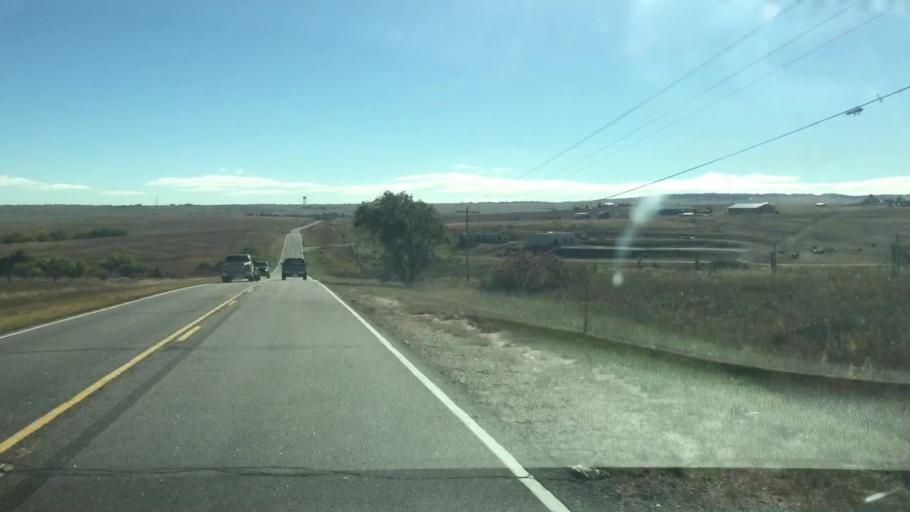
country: US
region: Colorado
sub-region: Elbert County
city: Kiowa
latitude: 39.3521
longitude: -104.4960
